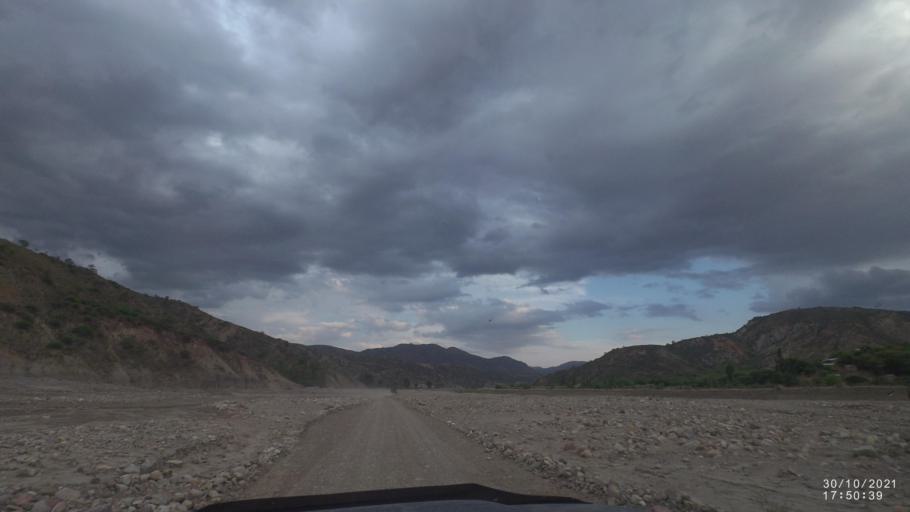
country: BO
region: Cochabamba
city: Sipe Sipe
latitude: -17.5364
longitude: -66.5085
